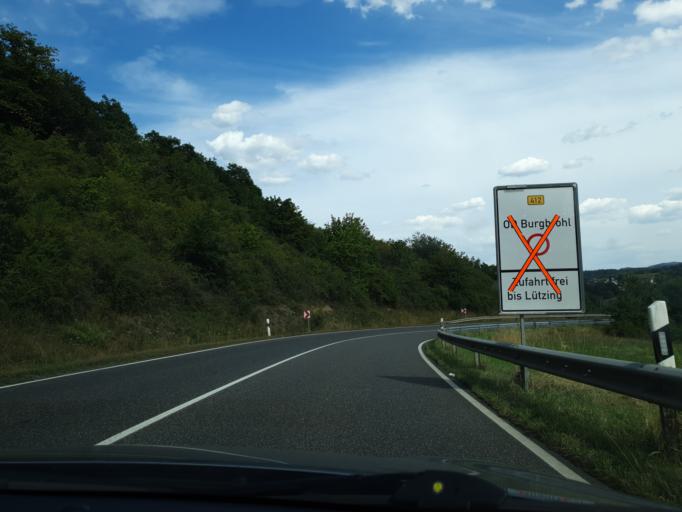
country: DE
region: Rheinland-Pfalz
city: Niederzissen
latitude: 50.4637
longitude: 7.2420
